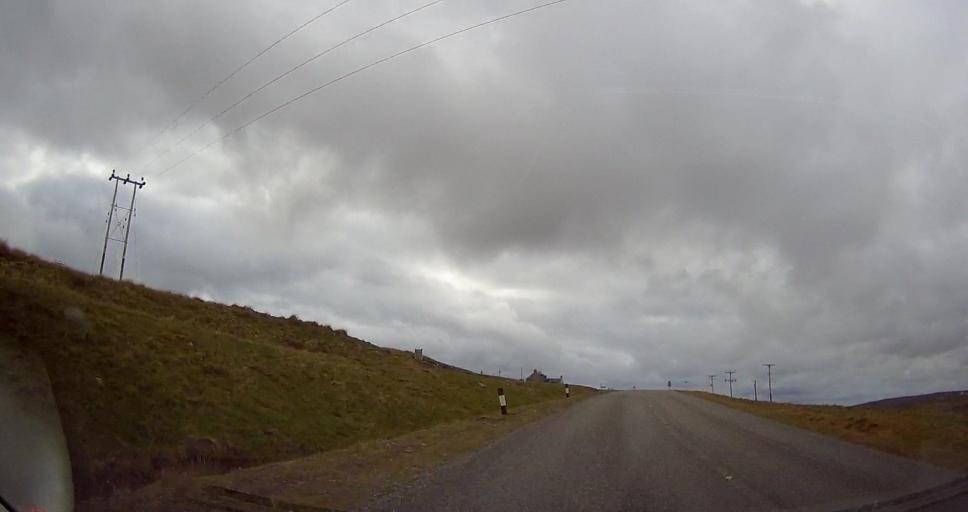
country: GB
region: Scotland
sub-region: Shetland Islands
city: Shetland
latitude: 60.6692
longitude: -1.0624
